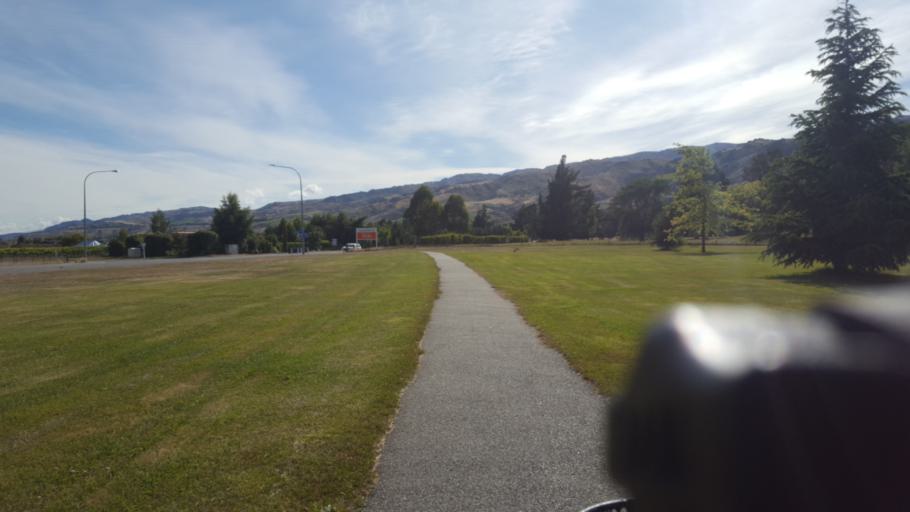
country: NZ
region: Otago
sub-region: Queenstown-Lakes District
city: Wanaka
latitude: -45.0349
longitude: 169.2015
